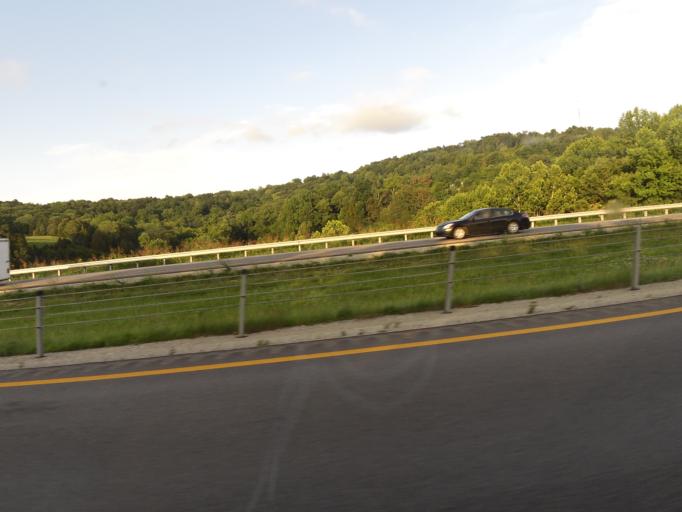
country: US
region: Kentucky
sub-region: Rockcastle County
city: Mount Vernon
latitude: 37.4130
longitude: -84.3409
